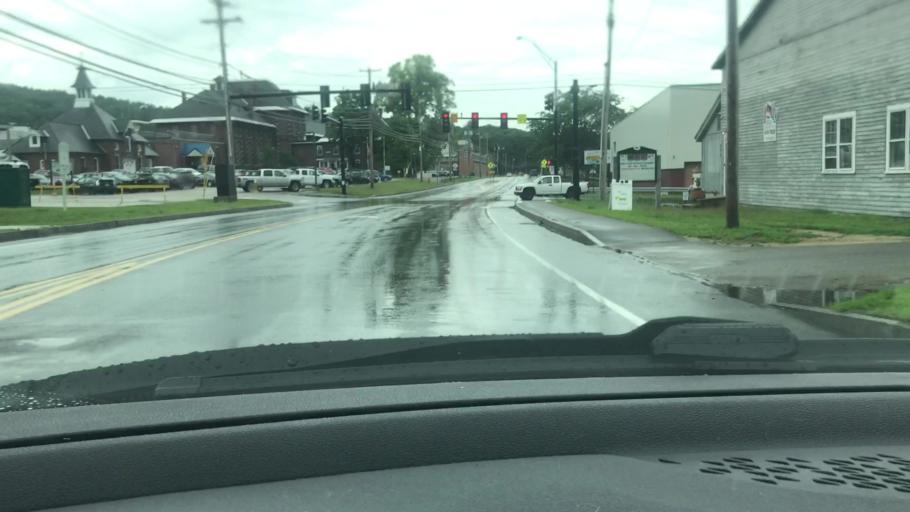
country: US
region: New Hampshire
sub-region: Merrimack County
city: East Concord
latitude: 43.2260
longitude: -71.5552
